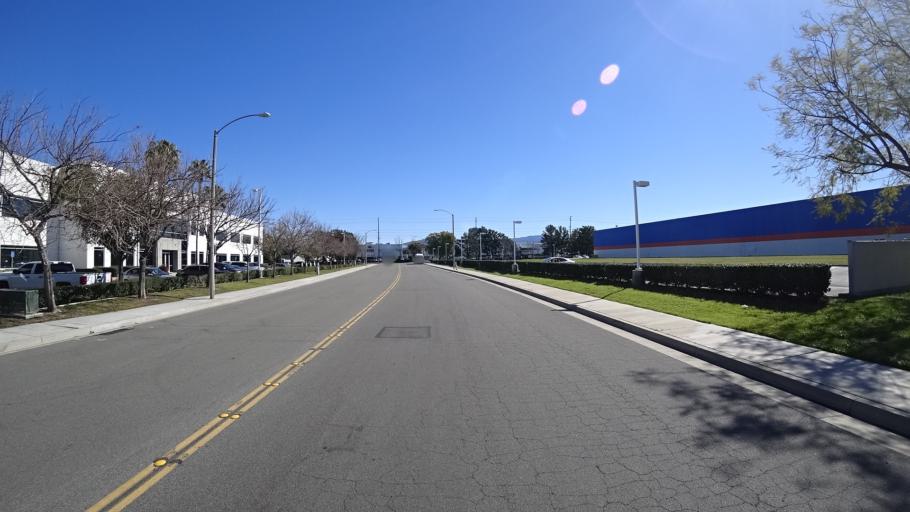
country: US
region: California
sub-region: Orange County
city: Yorba Linda
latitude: 33.8618
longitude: -117.8084
